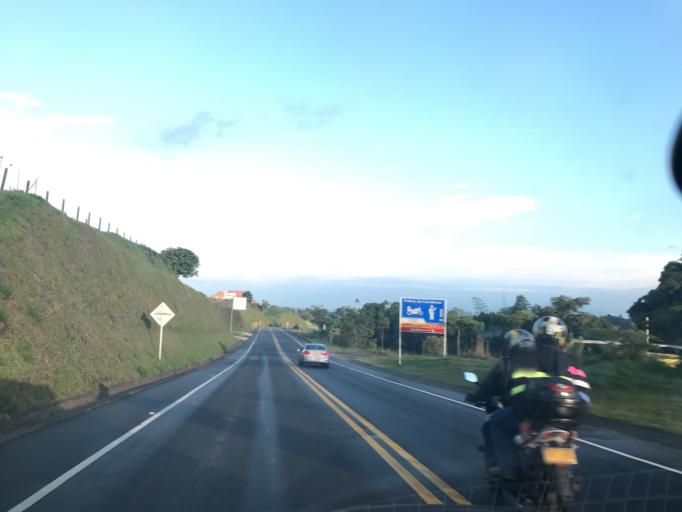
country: CO
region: Quindio
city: Filandia
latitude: 4.7444
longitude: -75.6689
